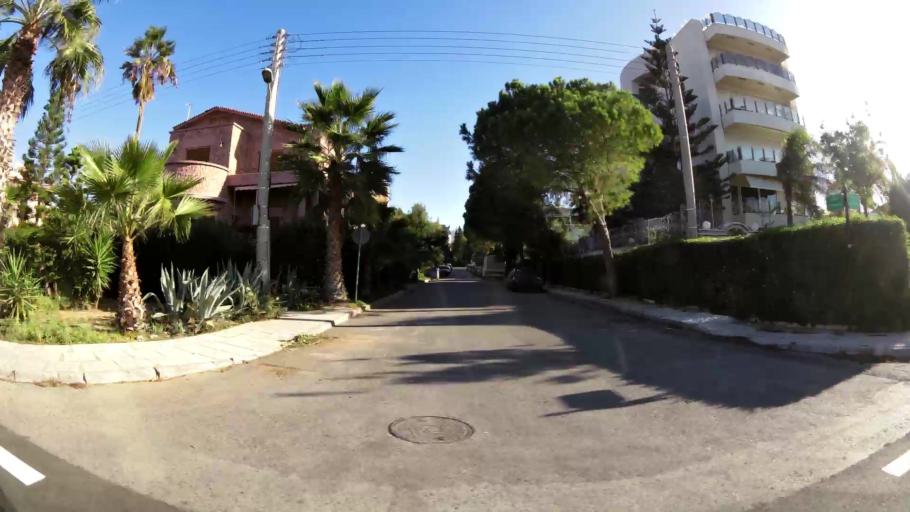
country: GR
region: Attica
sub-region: Nomarchia Athinas
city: Elliniko
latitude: 37.8672
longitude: 23.7397
